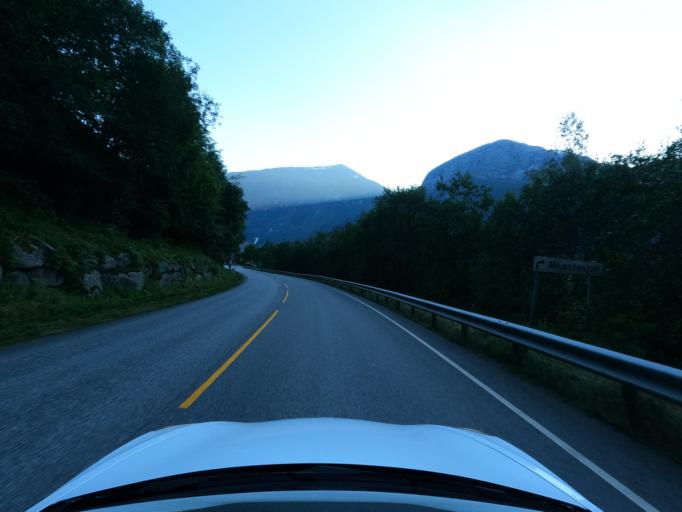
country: NO
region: Hordaland
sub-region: Odda
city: Odda
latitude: 60.1018
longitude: 6.5503
